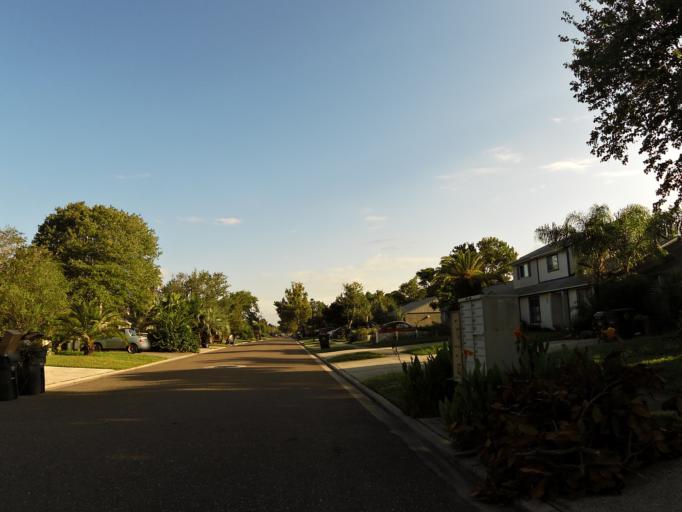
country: US
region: Florida
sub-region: Duval County
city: Atlantic Beach
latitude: 30.3290
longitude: -81.4140
